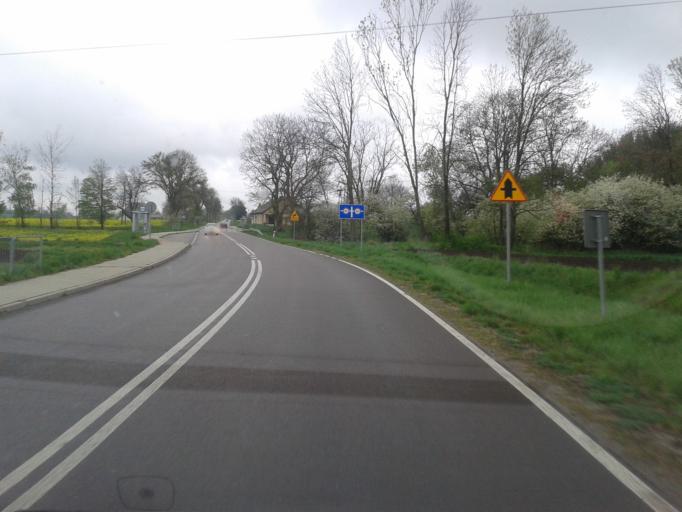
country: PL
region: Lublin Voivodeship
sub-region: Powiat hrubieszowski
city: Dolhobyczow
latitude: 50.5882
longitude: 23.9975
